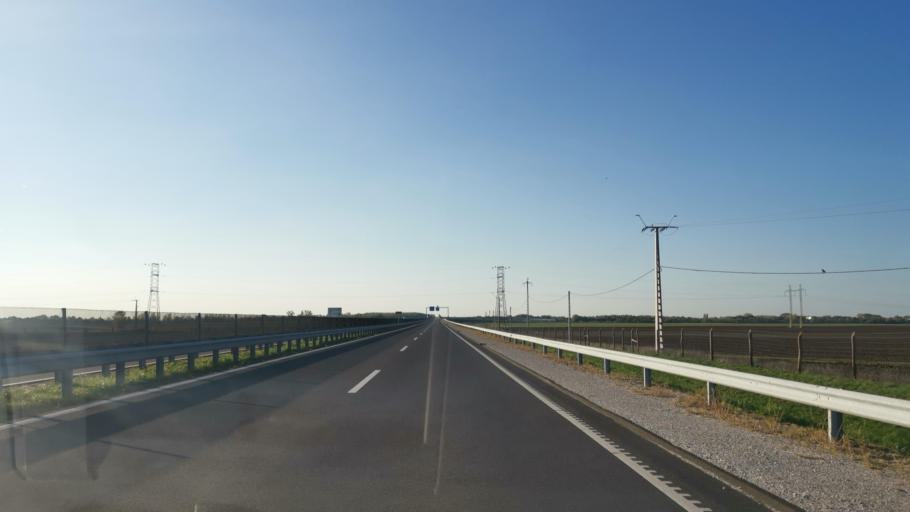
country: HU
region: Heves
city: Erdotelek
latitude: 47.7340
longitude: 20.3417
